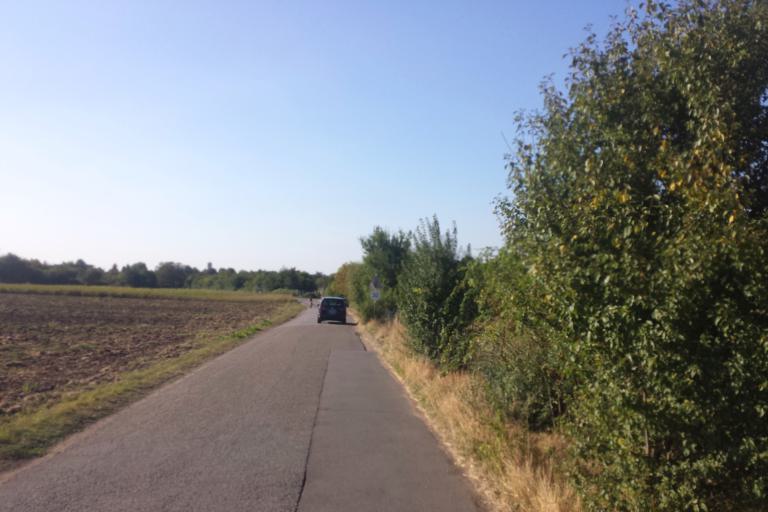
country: DE
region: Baden-Wuerttemberg
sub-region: Karlsruhe Region
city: Edingen-Neckarhausen
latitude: 49.4624
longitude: 8.6196
